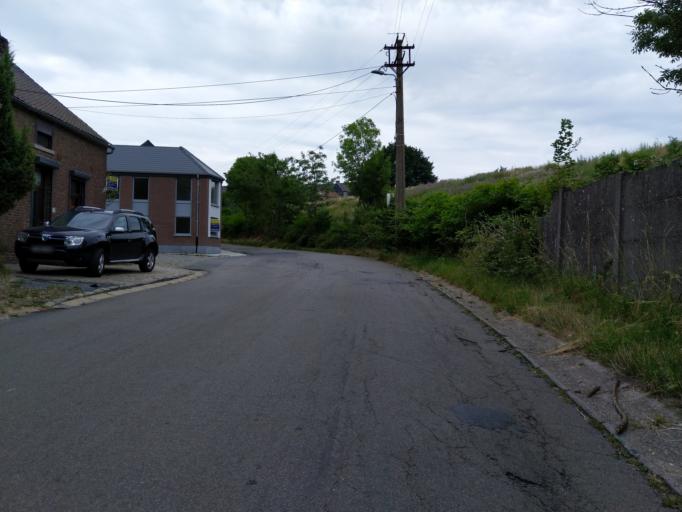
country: BE
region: Wallonia
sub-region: Province du Hainaut
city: Mons
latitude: 50.4919
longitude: 4.0130
